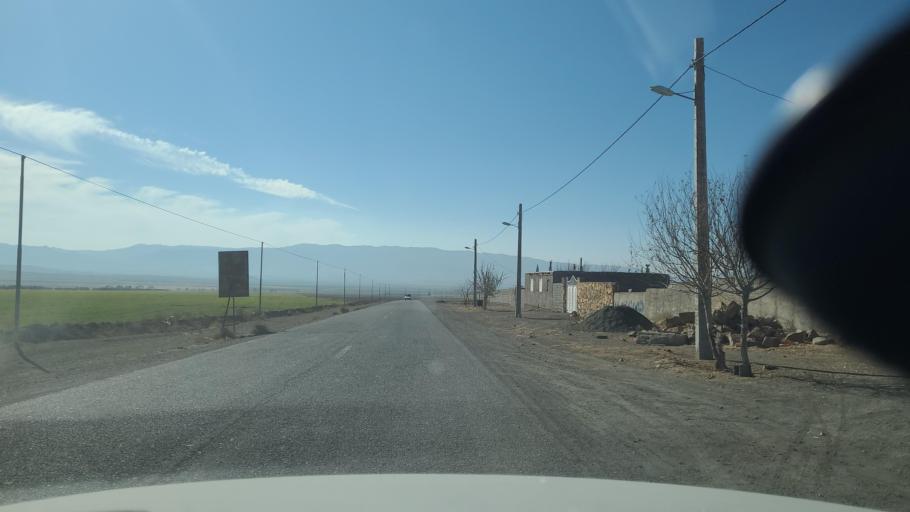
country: IR
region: Razavi Khorasan
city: Dowlatabad
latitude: 35.6167
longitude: 59.4749
